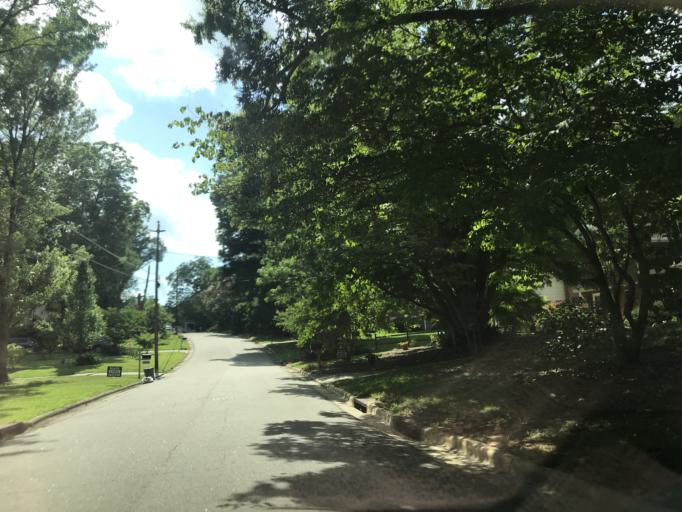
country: US
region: North Carolina
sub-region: Wake County
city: West Raleigh
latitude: 35.7788
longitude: -78.7107
